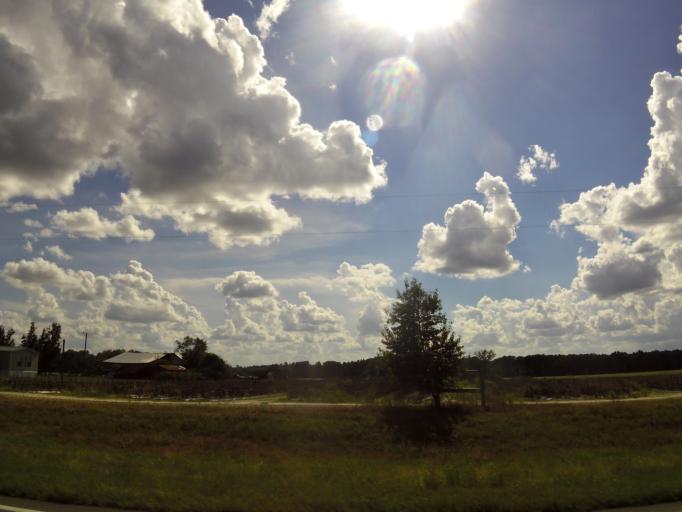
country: US
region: Georgia
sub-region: Echols County
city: Statenville
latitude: 30.7638
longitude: -83.1270
